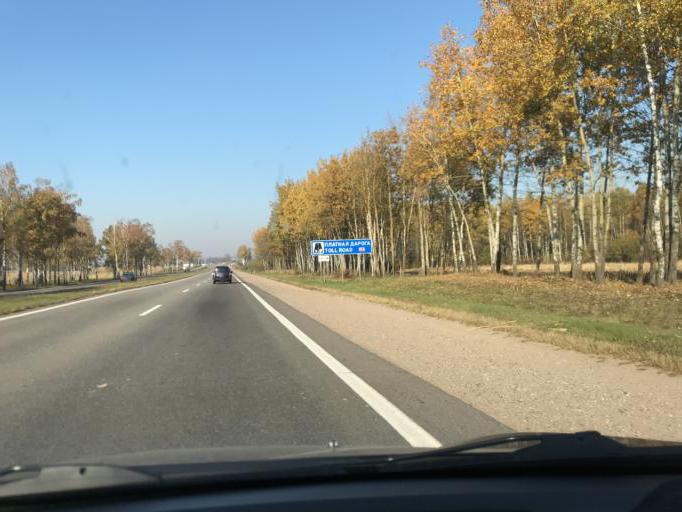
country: BY
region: Minsk
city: Luhavaya Slabada
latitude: 53.7814
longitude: 27.8243
